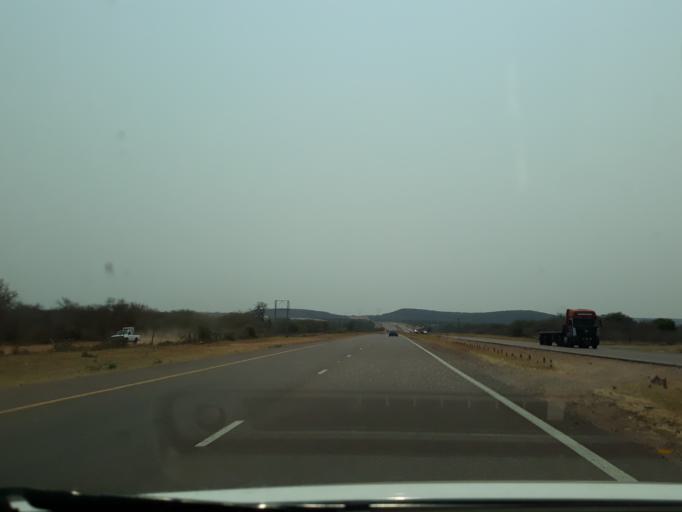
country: BW
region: Kgatleng
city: Bokaa
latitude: -24.4113
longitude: 26.0512
